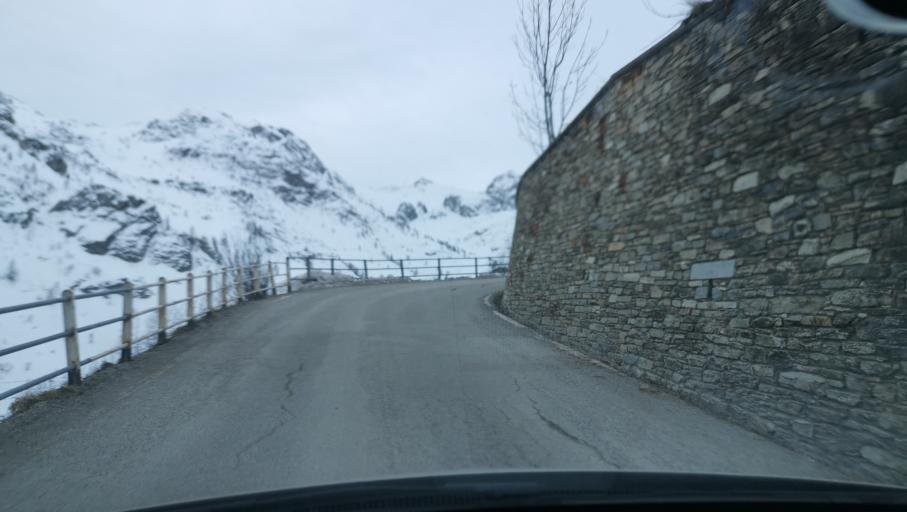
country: IT
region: Piedmont
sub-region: Provincia di Cuneo
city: Campomolino
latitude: 44.4002
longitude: 7.1739
